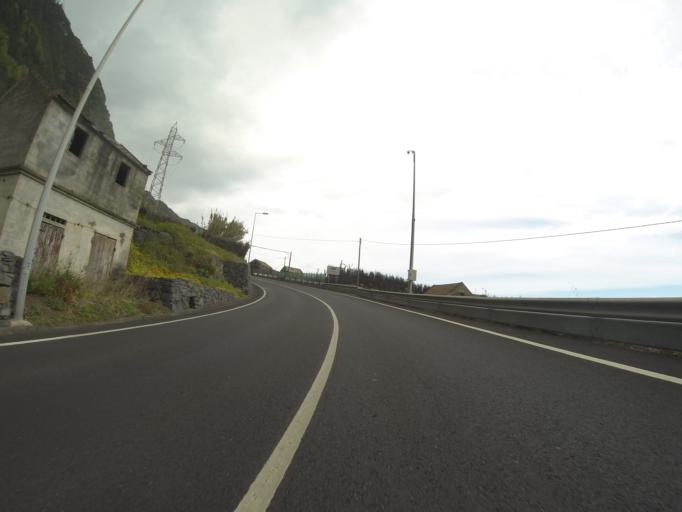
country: PT
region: Madeira
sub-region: Porto Moniz
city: Porto Moniz
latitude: 32.8437
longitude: -17.1445
